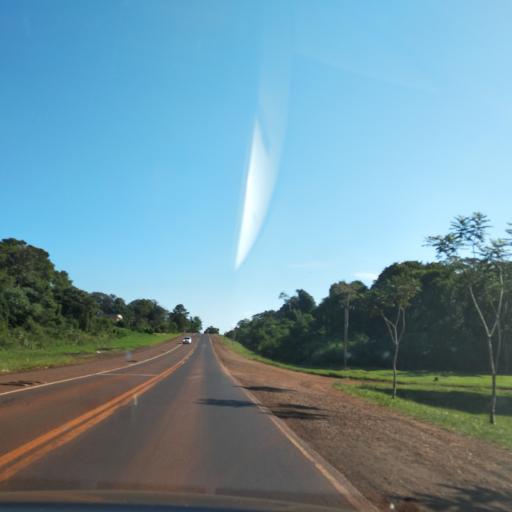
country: AR
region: Misiones
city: Jardin America
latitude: -27.0523
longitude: -55.2501
